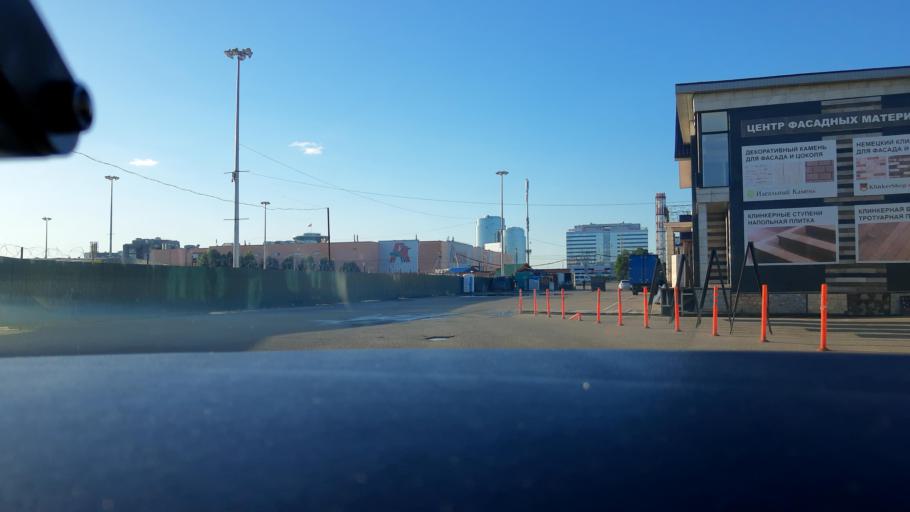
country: RU
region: Moscow
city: Strogino
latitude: 55.8072
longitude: 37.3842
